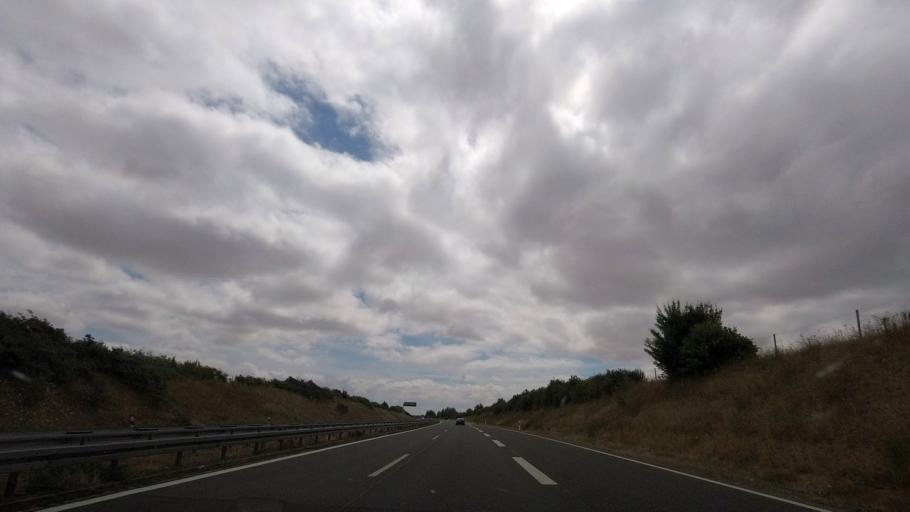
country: DE
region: Brandenburg
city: Schenkenberg
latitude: 53.3557
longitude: 13.9742
